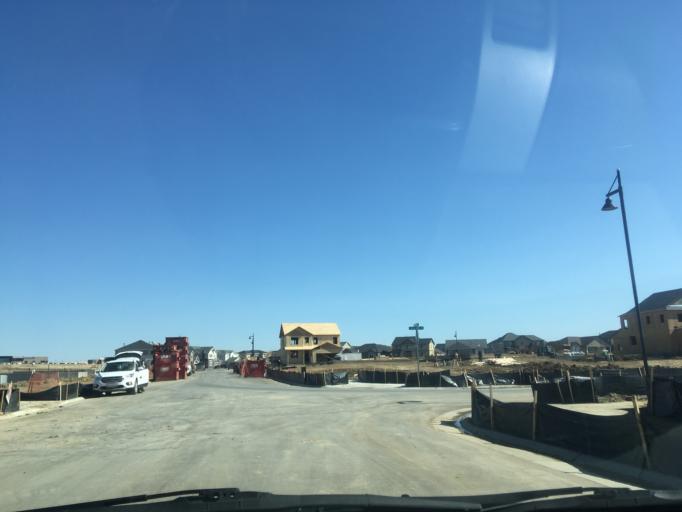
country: US
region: Colorado
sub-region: Boulder County
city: Erie
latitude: 40.0548
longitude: -105.0297
